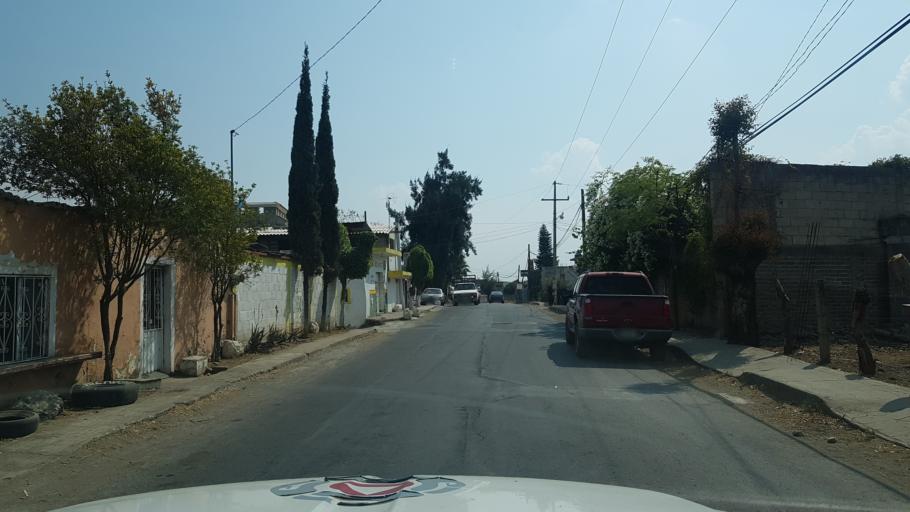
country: MX
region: Morelos
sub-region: Yecapixtla
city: Yecapixtla
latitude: 18.8864
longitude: -98.8658
